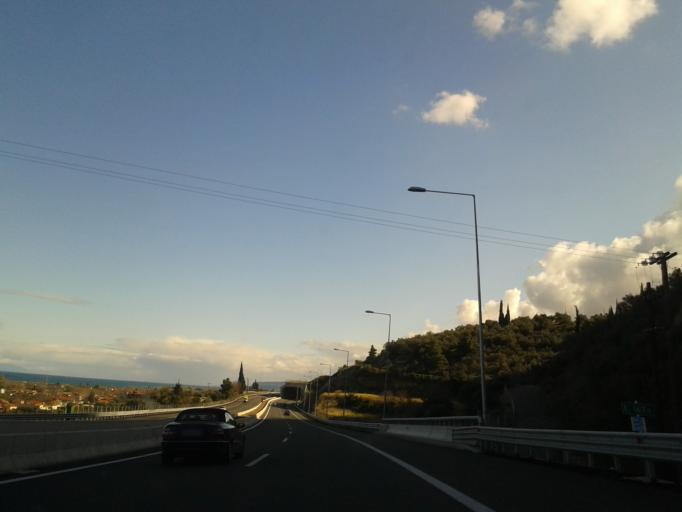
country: GR
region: West Greece
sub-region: Nomos Achaias
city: Temeni
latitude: 38.2096
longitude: 22.1299
